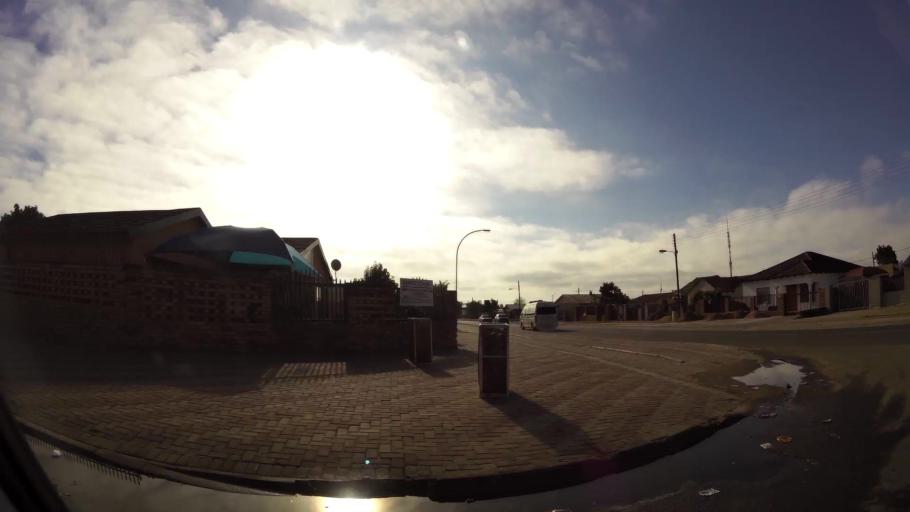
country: ZA
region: Limpopo
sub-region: Capricorn District Municipality
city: Polokwane
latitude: -23.8457
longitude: 29.3871
